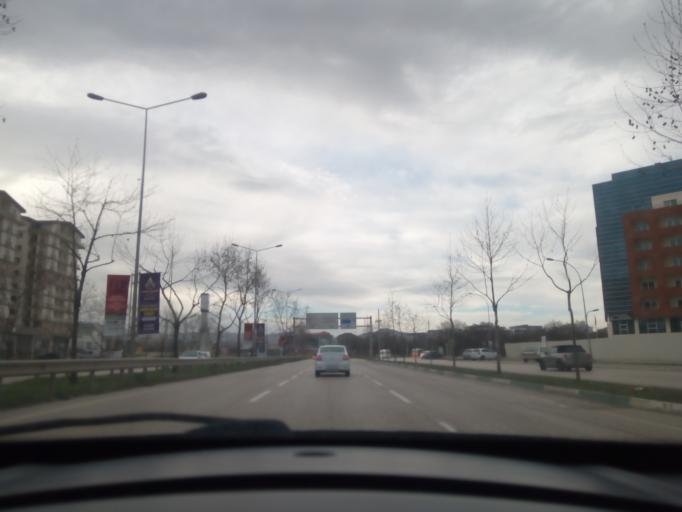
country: TR
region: Bursa
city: Cali
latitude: 40.2167
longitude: 28.9521
